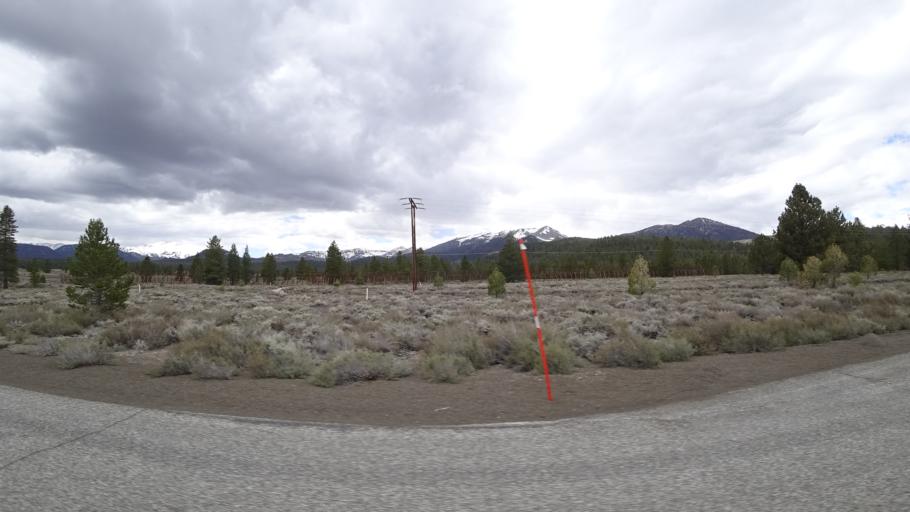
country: US
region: California
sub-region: Mono County
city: Mammoth Lakes
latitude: 37.7495
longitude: -118.9832
